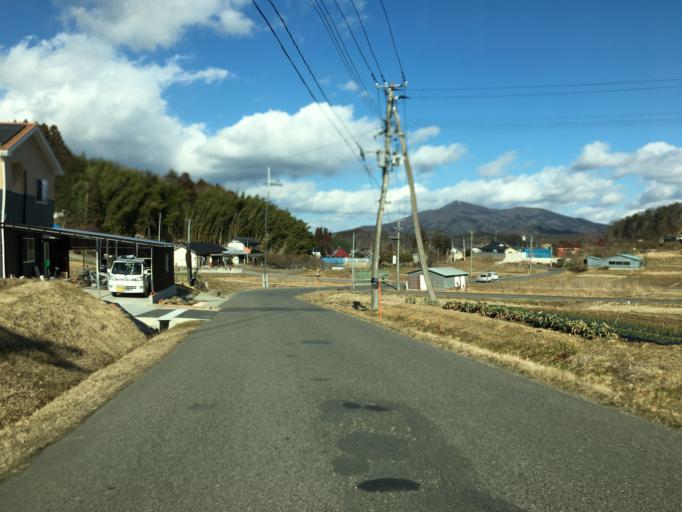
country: JP
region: Fukushima
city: Funehikimachi-funehiki
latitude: 37.4350
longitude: 140.5596
